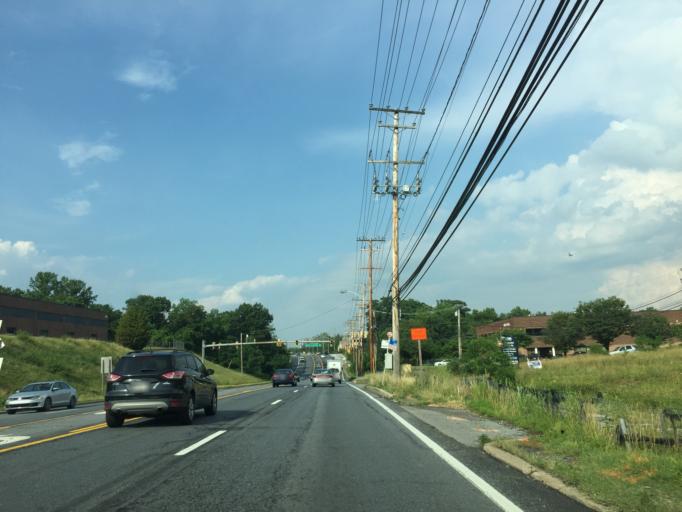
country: US
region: Maryland
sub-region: Anne Arundel County
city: Jessup
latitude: 39.1748
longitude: -76.7780
